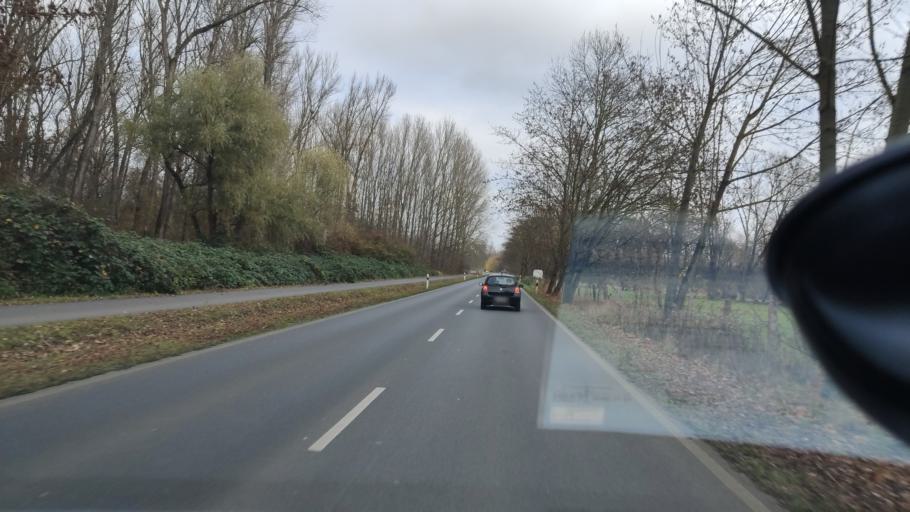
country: DE
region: Lower Saxony
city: Hemmingen
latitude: 52.3278
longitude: 9.7508
